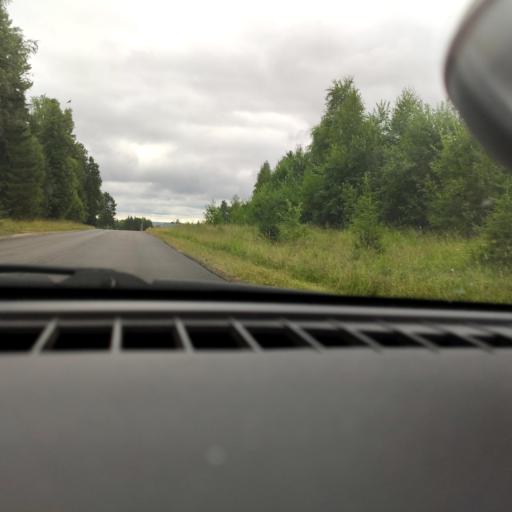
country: RU
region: Perm
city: Polazna
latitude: 58.3411
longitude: 56.2222
